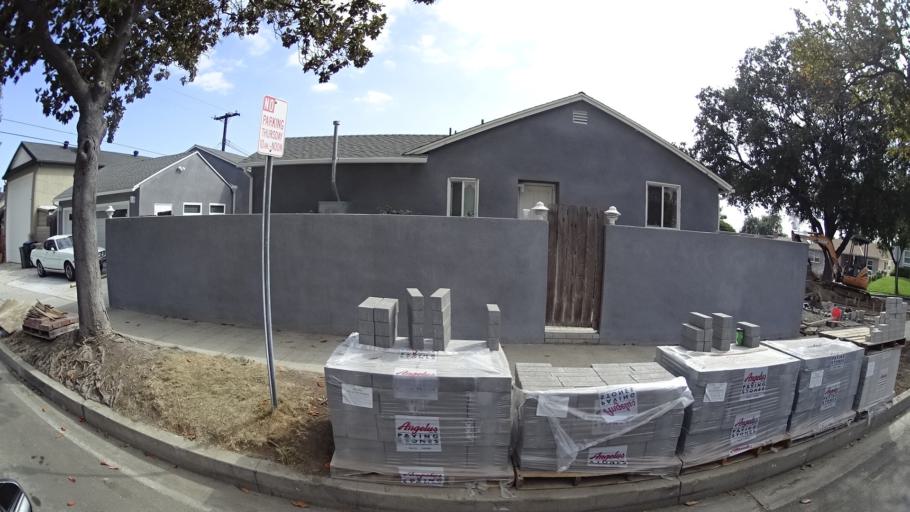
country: US
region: California
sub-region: Los Angeles County
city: Burbank
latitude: 34.1992
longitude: -118.3171
